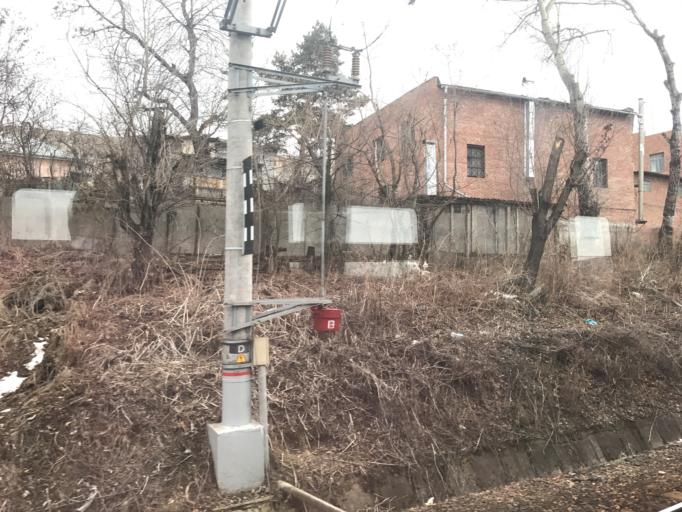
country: RU
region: Stavropol'skiy
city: Kislovodsk
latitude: 43.9082
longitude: 42.7195
